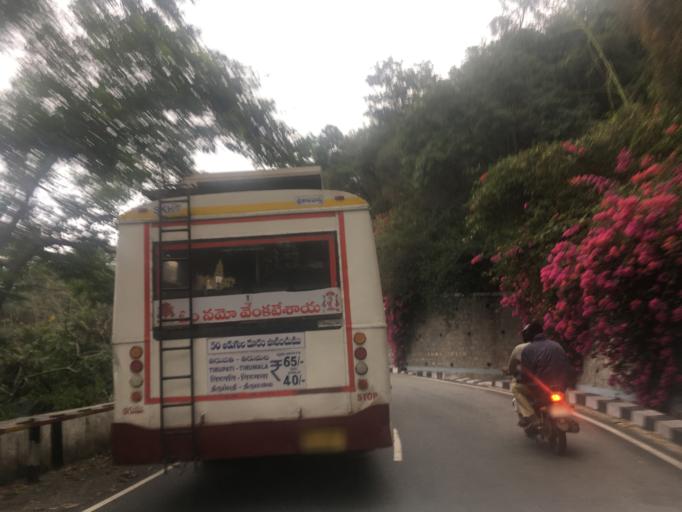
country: IN
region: Andhra Pradesh
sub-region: Chittoor
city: Tirumala
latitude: 13.6660
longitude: 79.3509
